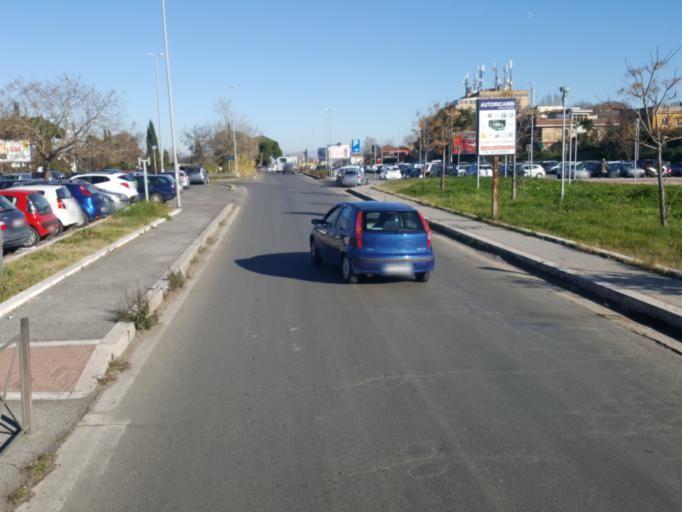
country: IT
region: Latium
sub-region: Citta metropolitana di Roma Capitale
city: Acilia-Castel Fusano-Ostia Antica
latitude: 41.7840
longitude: 12.3610
